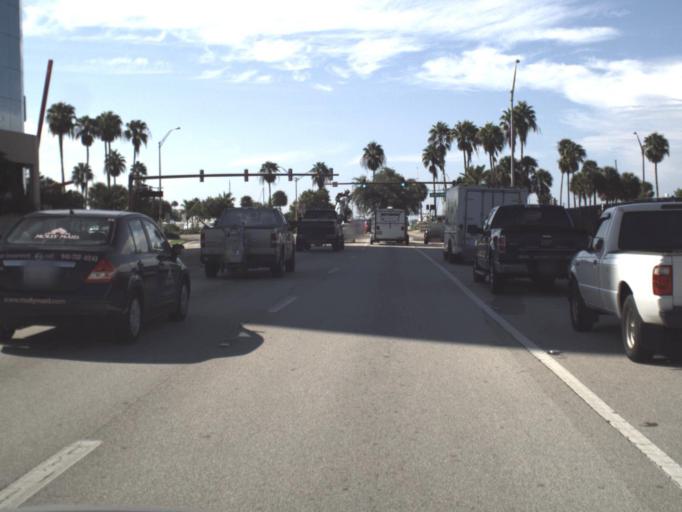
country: US
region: Florida
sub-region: Sarasota County
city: Sarasota
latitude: 27.3367
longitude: -82.5469
